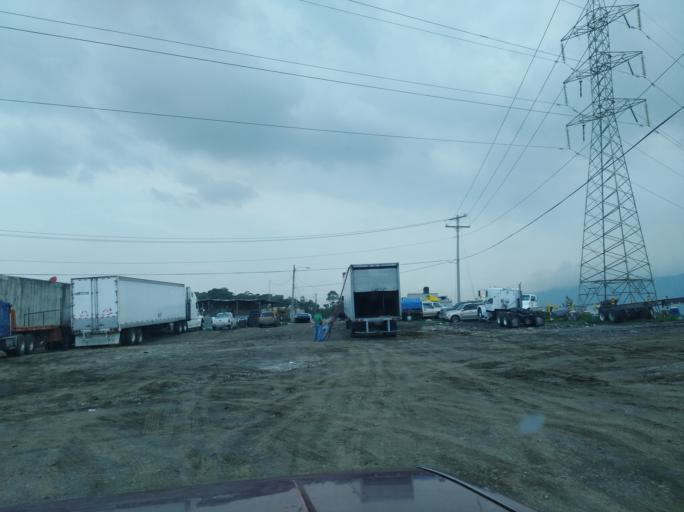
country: GT
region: Guatemala
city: Villa Nueva
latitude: 14.5228
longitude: -90.6207
